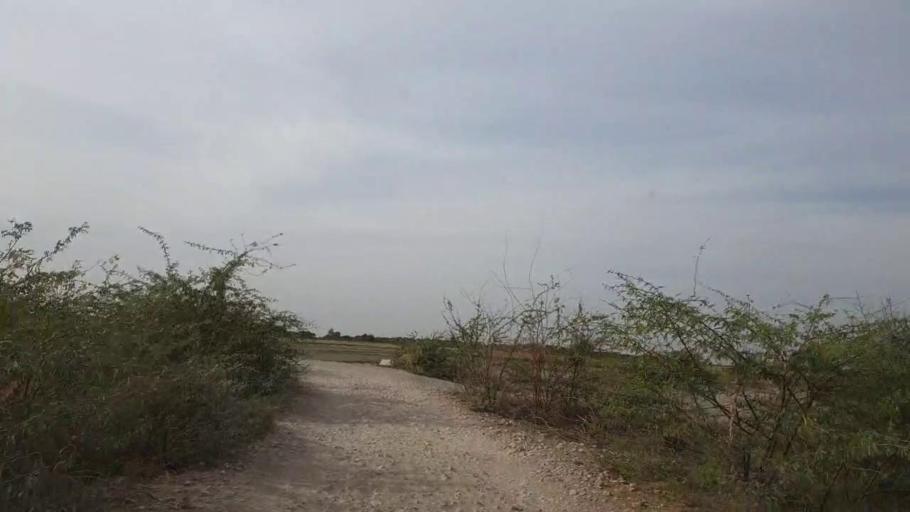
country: PK
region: Sindh
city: Nabisar
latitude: 25.0000
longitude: 69.5424
